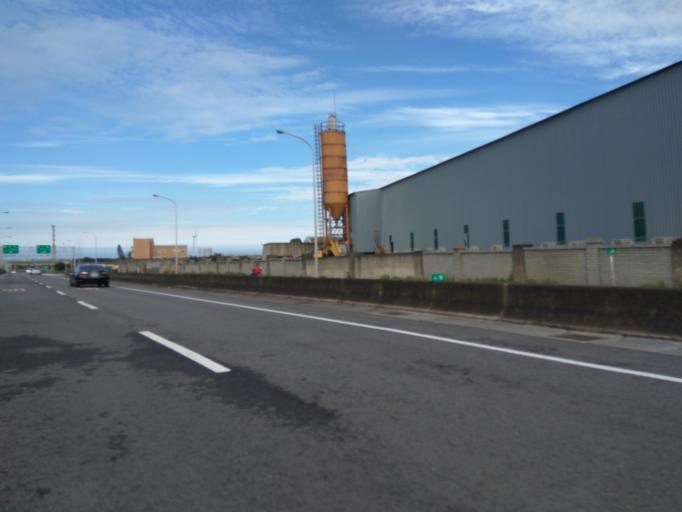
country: TW
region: Taiwan
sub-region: Hsinchu
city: Zhubei
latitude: 25.0272
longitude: 121.0582
